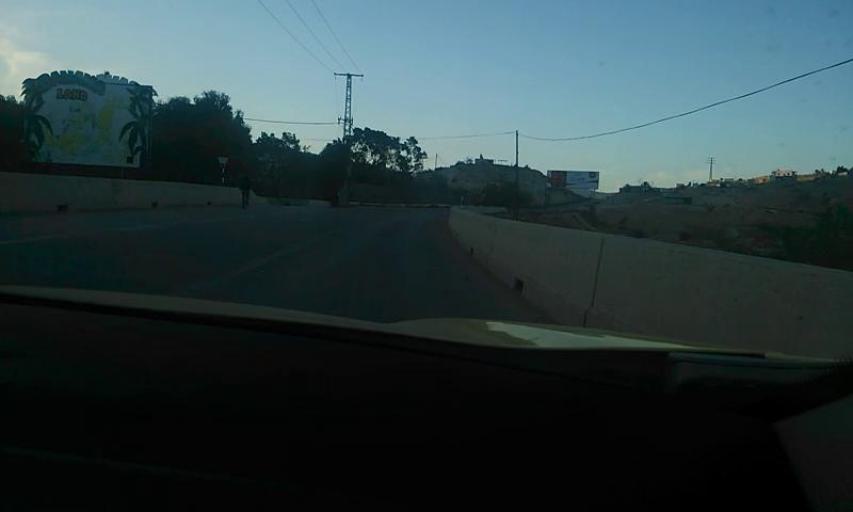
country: PS
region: West Bank
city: An Nuway`imah
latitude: 31.8994
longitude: 35.4274
